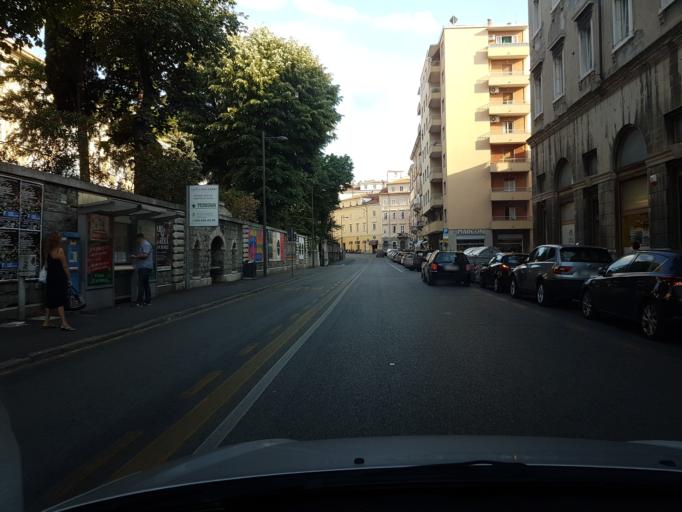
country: IT
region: Friuli Venezia Giulia
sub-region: Provincia di Trieste
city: Trieste
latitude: 45.6495
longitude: 13.7805
